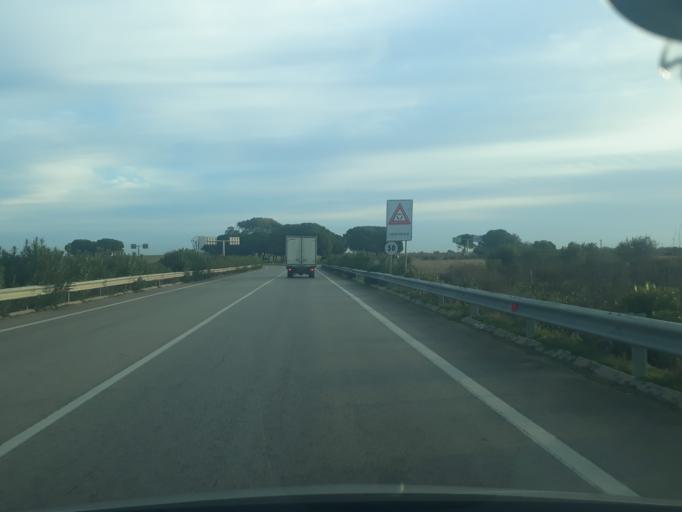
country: IT
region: Apulia
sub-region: Provincia di Brindisi
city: Brindisi
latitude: 40.6637
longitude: 17.9181
